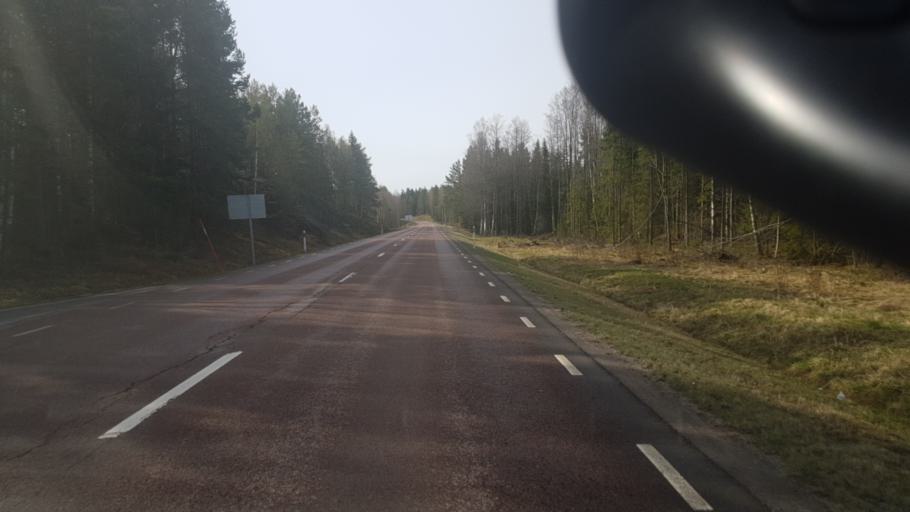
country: SE
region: Vaermland
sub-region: Arvika Kommun
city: Arvika
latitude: 59.6248
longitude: 12.6177
